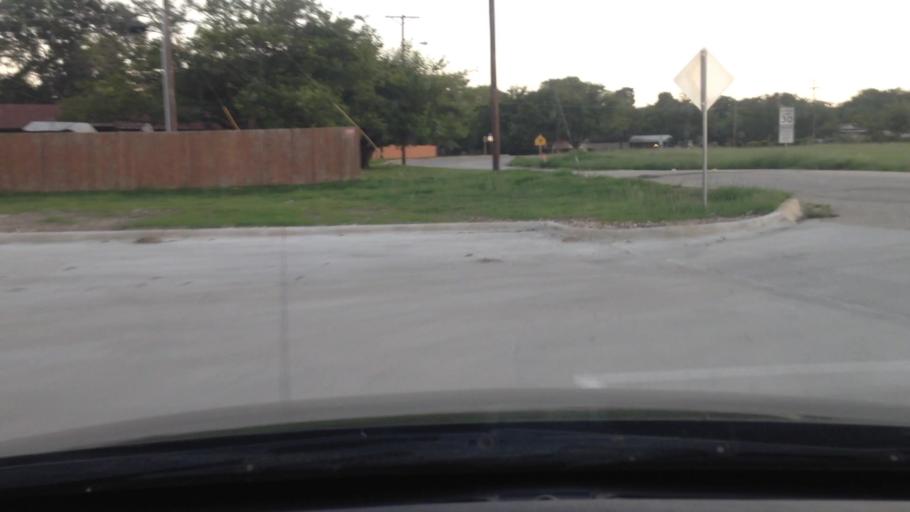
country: US
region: Texas
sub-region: Tarrant County
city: White Settlement
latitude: 32.7778
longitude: -97.4670
